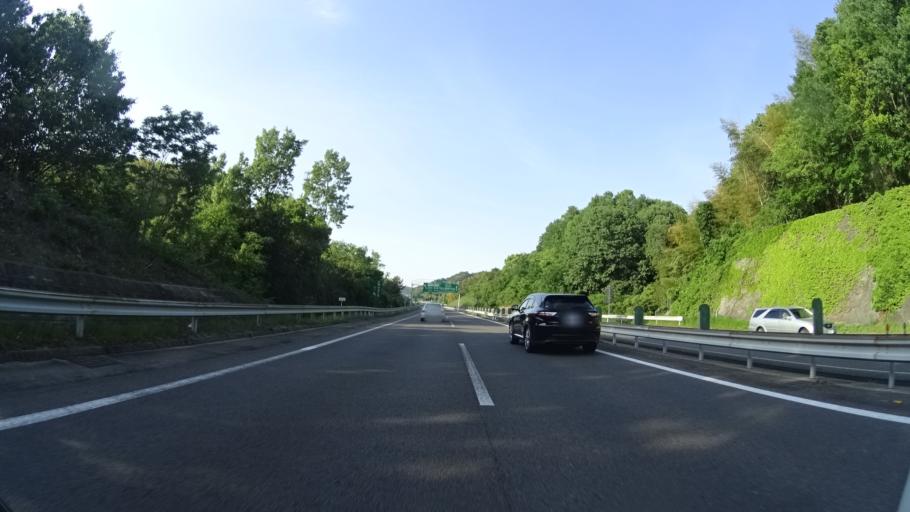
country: JP
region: Ehime
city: Kawanoecho
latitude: 33.9941
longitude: 133.5952
